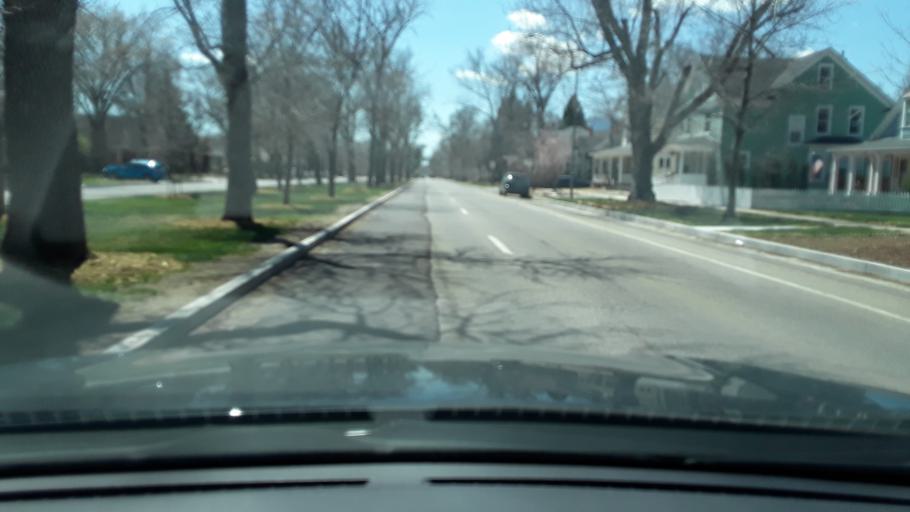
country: US
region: Colorado
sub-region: El Paso County
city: Colorado Springs
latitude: 38.8626
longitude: -104.8203
